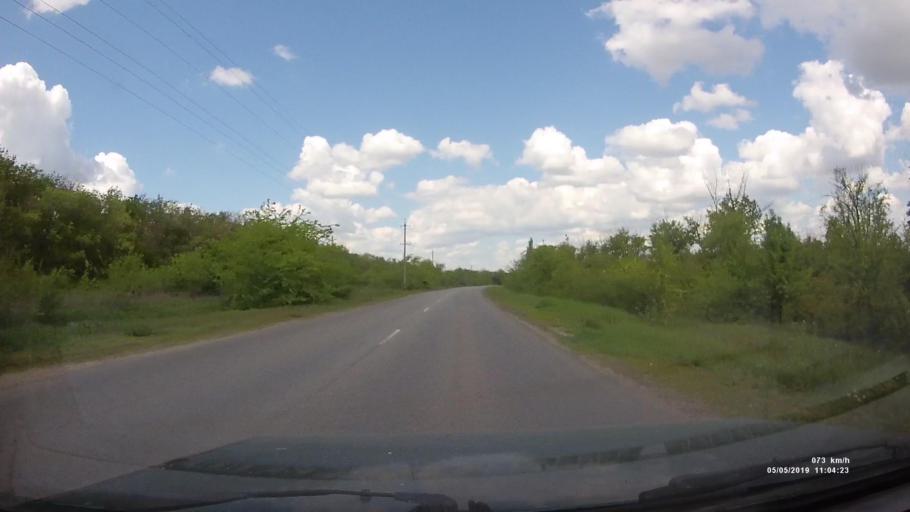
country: RU
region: Rostov
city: Ust'-Donetskiy
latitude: 47.6969
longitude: 40.9187
